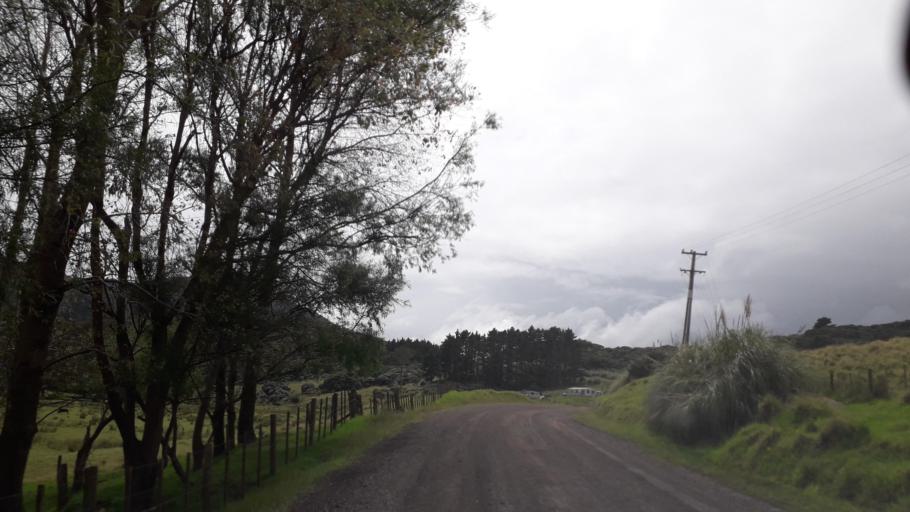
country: NZ
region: Northland
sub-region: Far North District
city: Ahipara
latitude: -35.4383
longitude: 173.3282
